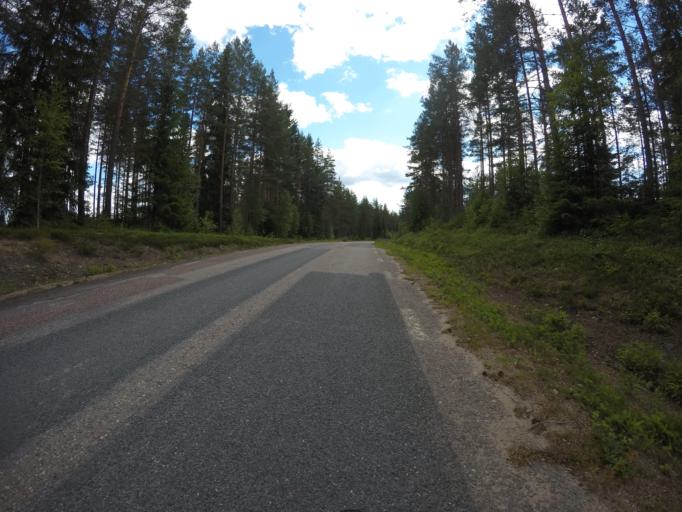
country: SE
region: OErebro
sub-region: Hallefors Kommun
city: Haellefors
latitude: 60.0705
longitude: 14.4925
